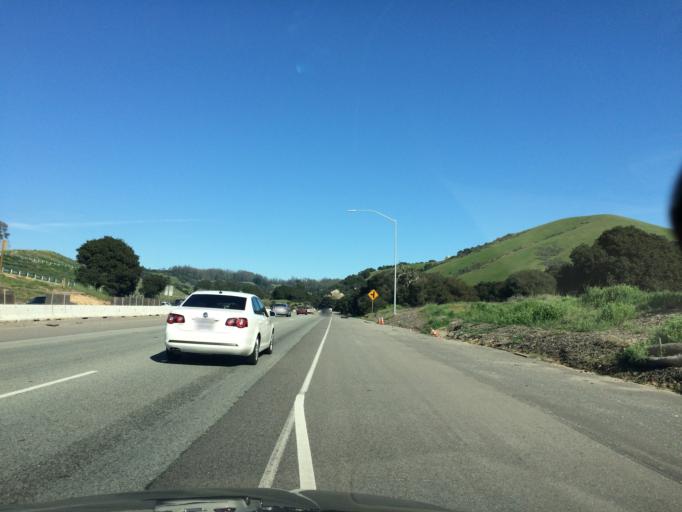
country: US
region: California
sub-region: San Benito County
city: Aromas
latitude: 36.8583
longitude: -121.6269
